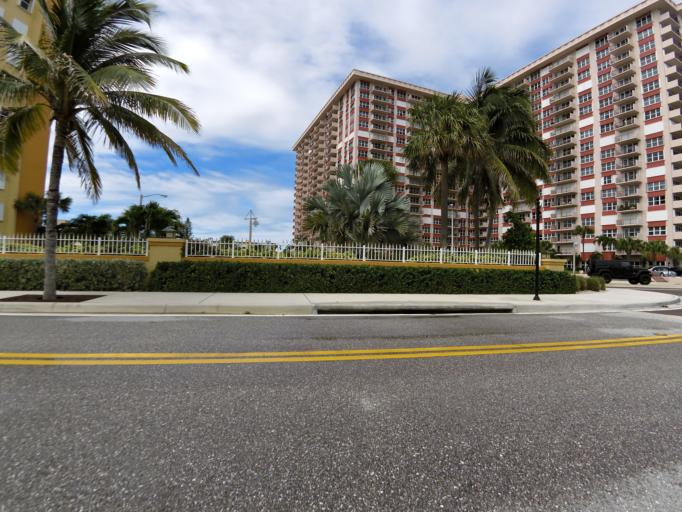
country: US
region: Florida
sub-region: Broward County
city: Terra Mar
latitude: 26.2382
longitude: -80.0887
